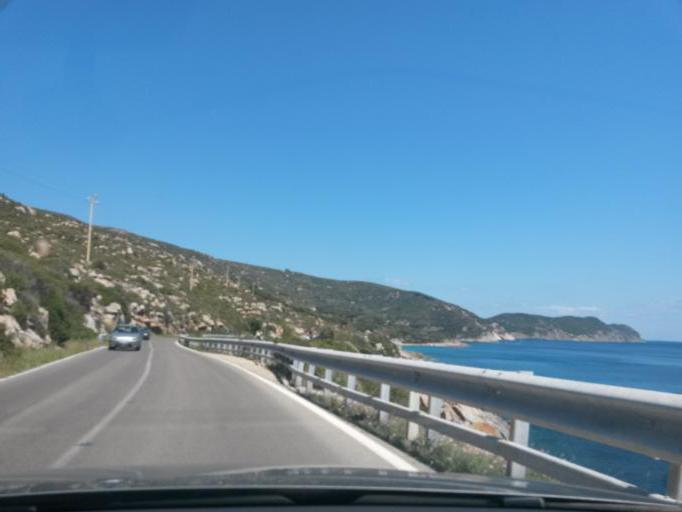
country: IT
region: Tuscany
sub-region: Provincia di Livorno
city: Marciana
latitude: 42.7332
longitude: 10.1668
